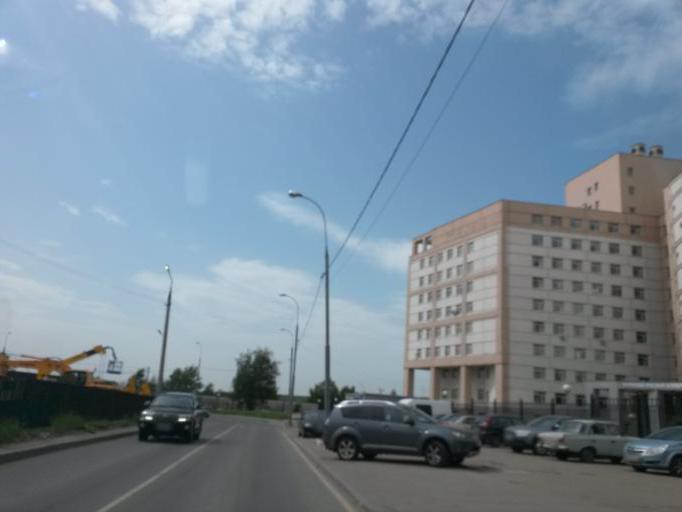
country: RU
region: Moscow
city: Chertanovo Yuzhnoye
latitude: 55.5813
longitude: 37.5850
